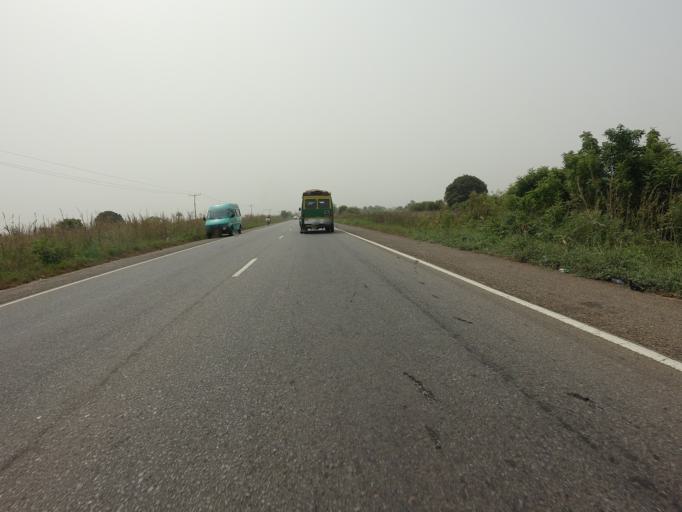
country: GH
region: Volta
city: Anloga
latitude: 5.9190
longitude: 0.5229
